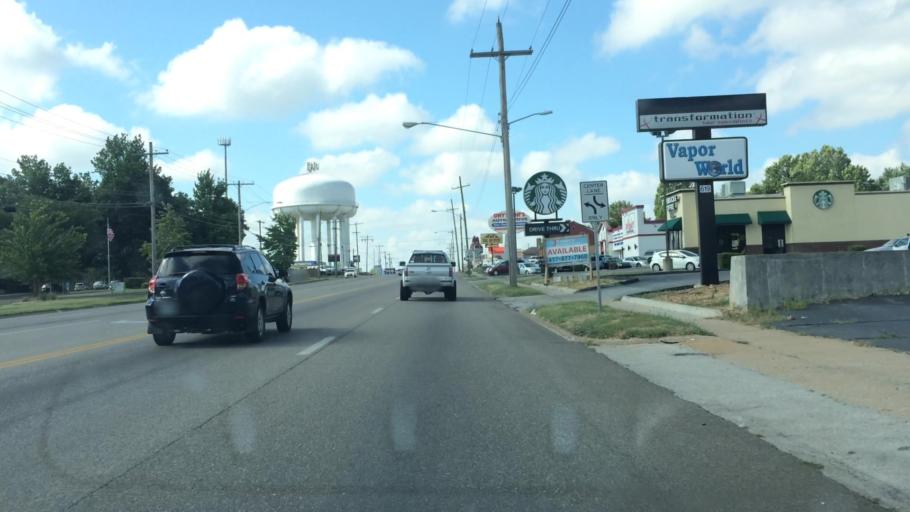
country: US
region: Missouri
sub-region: Greene County
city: Springfield
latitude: 37.2033
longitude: -93.2620
